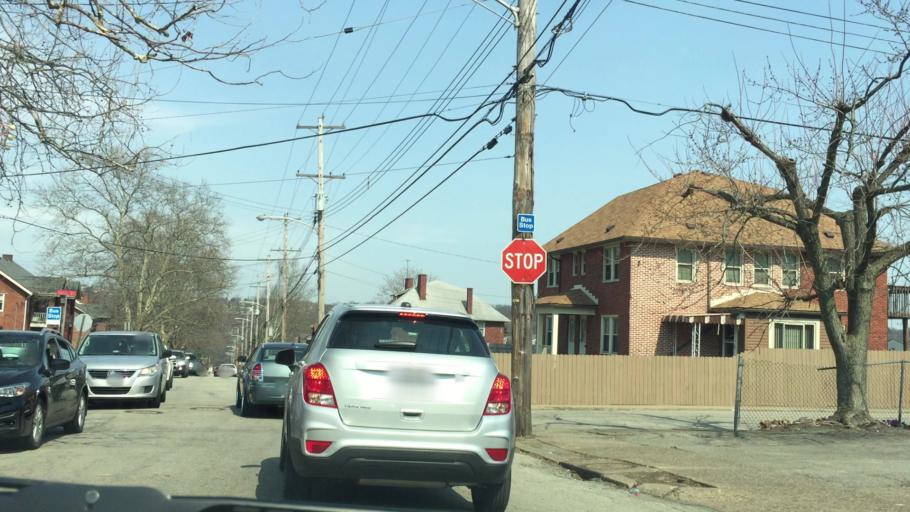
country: US
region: Pennsylvania
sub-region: Allegheny County
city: West Mifflin
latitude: 40.3635
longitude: -79.8508
